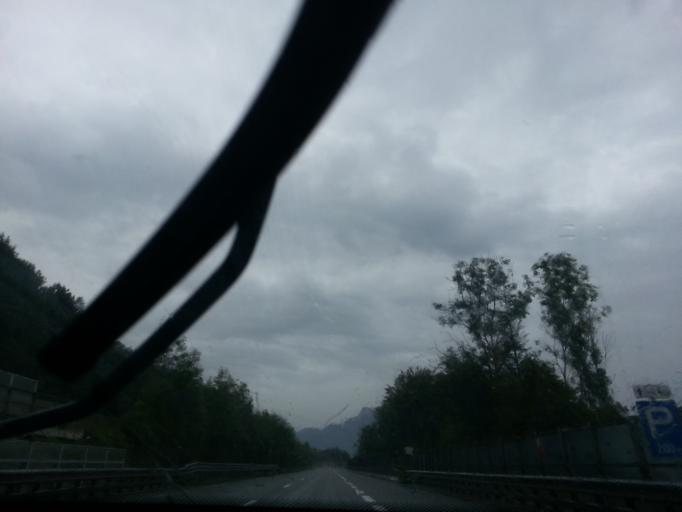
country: AT
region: Upper Austria
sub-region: Politischer Bezirk Vocklabruck
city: Mondsee
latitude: 47.8582
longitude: 13.3537
